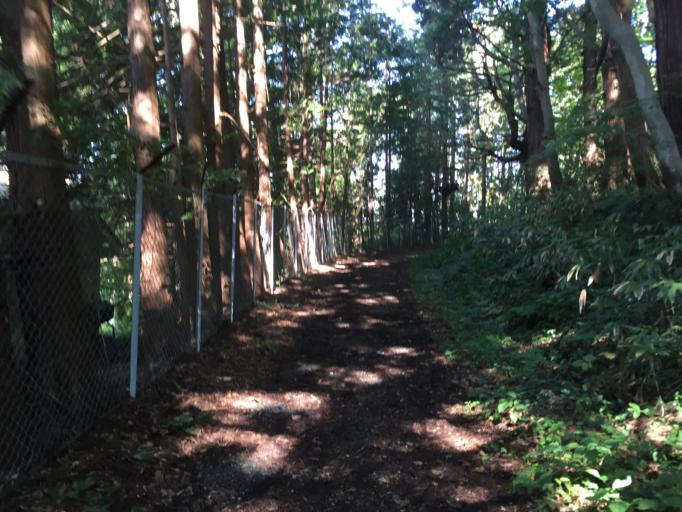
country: JP
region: Fukushima
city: Inawashiro
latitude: 37.4858
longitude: 139.9542
